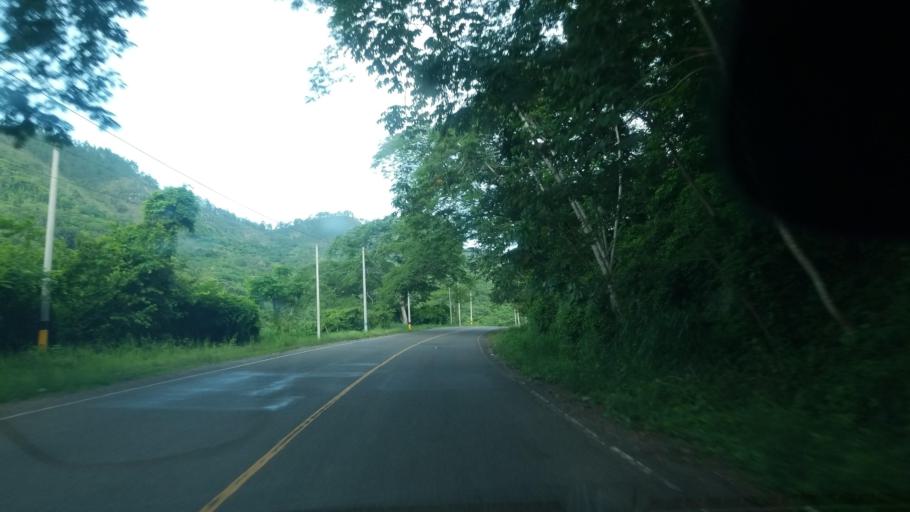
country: HN
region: Santa Barbara
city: Trinidad
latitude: 15.1087
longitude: -88.2042
